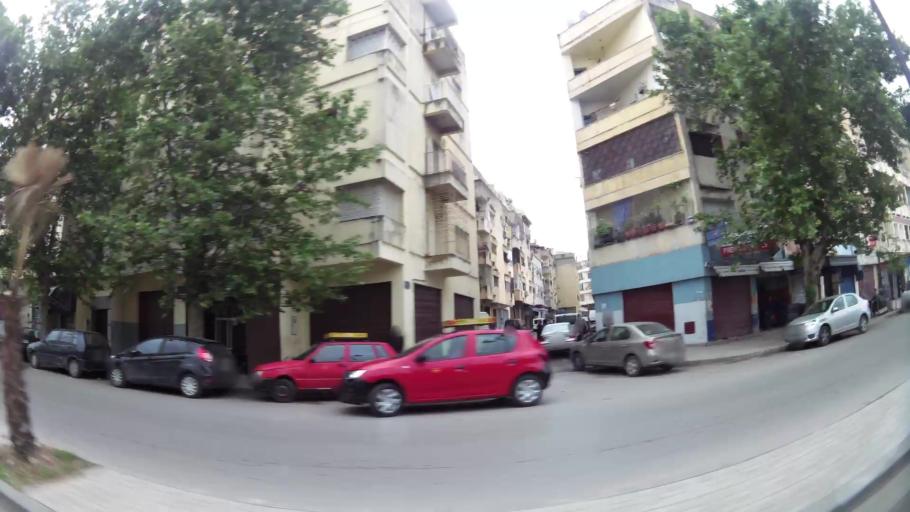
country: MA
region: Fes-Boulemane
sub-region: Fes
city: Fes
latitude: 34.0438
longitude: -5.0117
